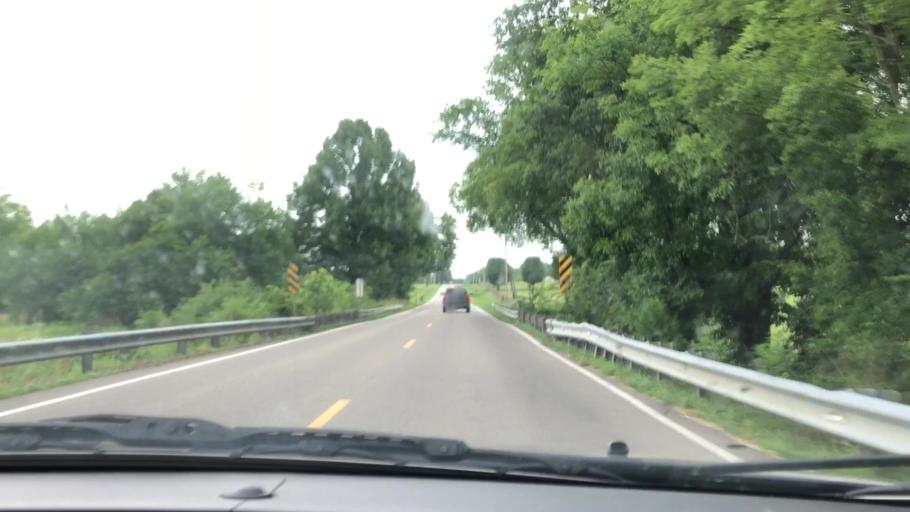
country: US
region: Tennessee
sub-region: Maury County
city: Spring Hill
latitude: 35.7310
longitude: -87.0111
